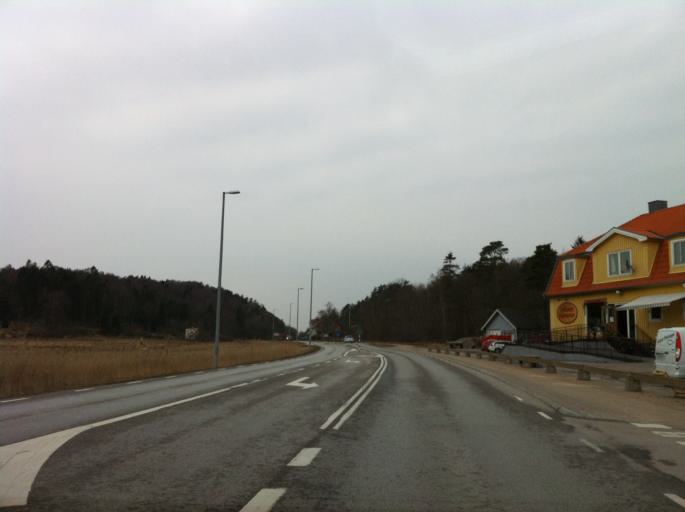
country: SE
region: Vaestra Goetaland
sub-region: Orust
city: Henan
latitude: 58.2245
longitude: 11.6863
